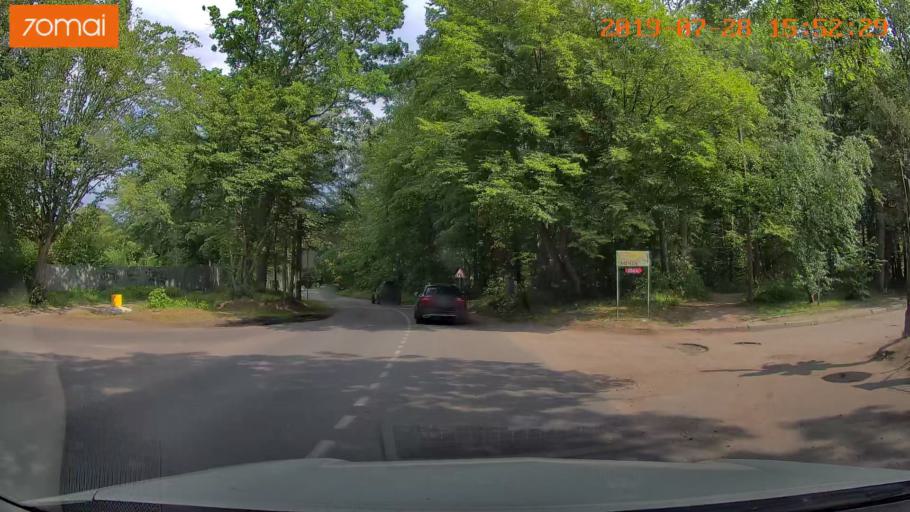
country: RU
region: Kaliningrad
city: Otradnoye
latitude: 54.9401
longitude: 20.1140
